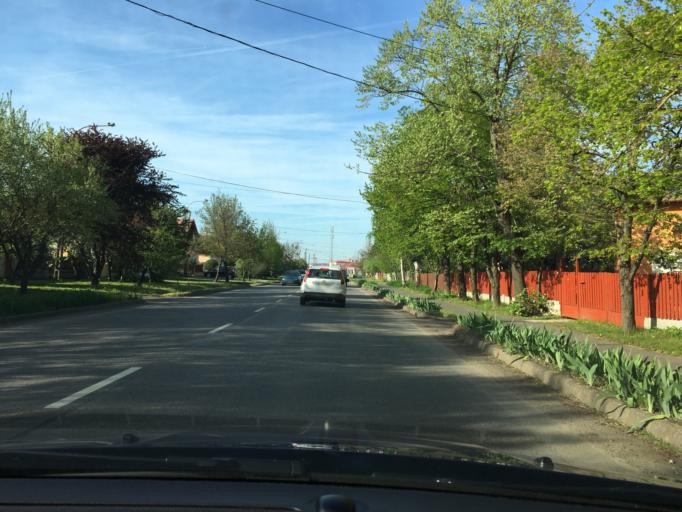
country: HU
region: Bekes
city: Korosladany
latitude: 46.9650
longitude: 21.0879
